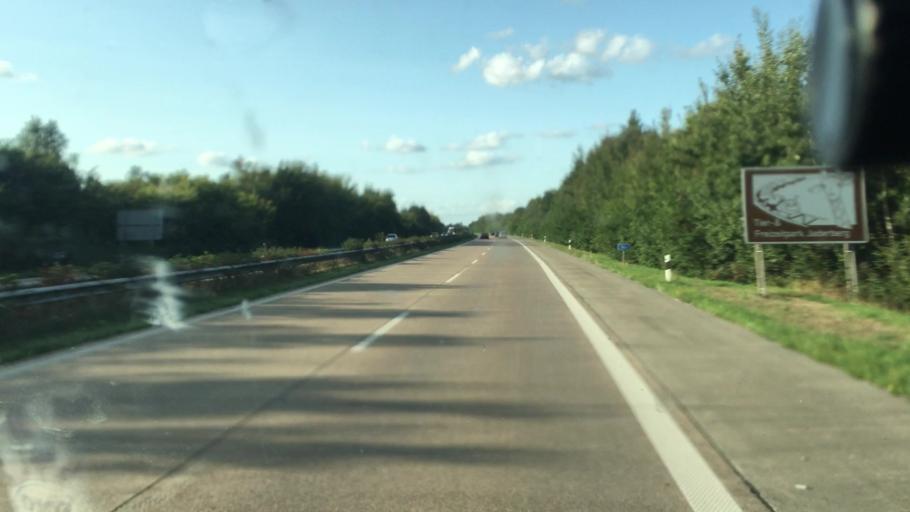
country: DE
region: Lower Saxony
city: Wiefelstede
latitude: 53.3076
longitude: 8.1444
